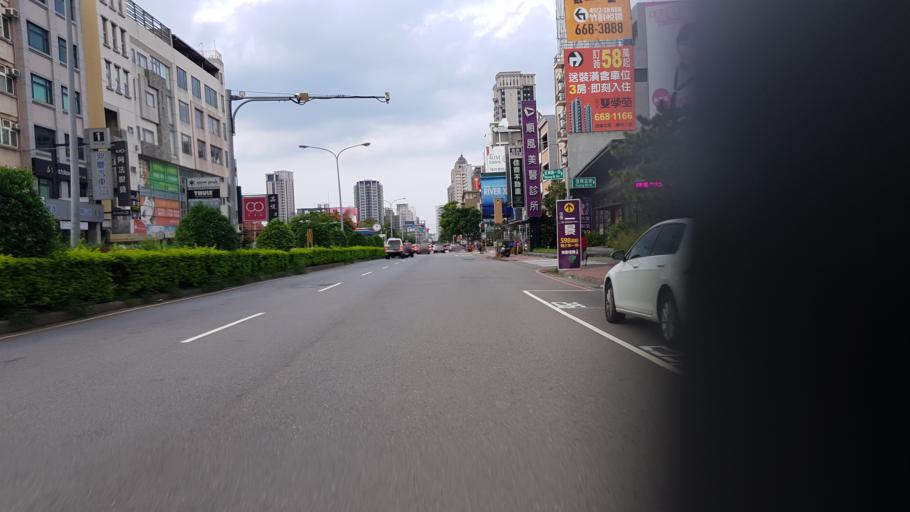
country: TW
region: Taiwan
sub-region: Hsinchu
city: Zhubei
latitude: 24.8125
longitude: 121.0251
